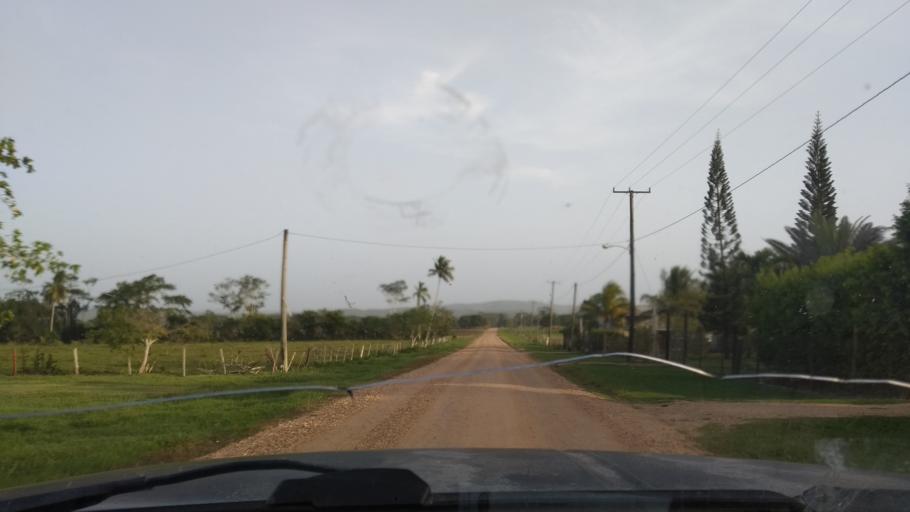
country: BZ
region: Cayo
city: San Ignacio
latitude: 17.2165
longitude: -89.0137
